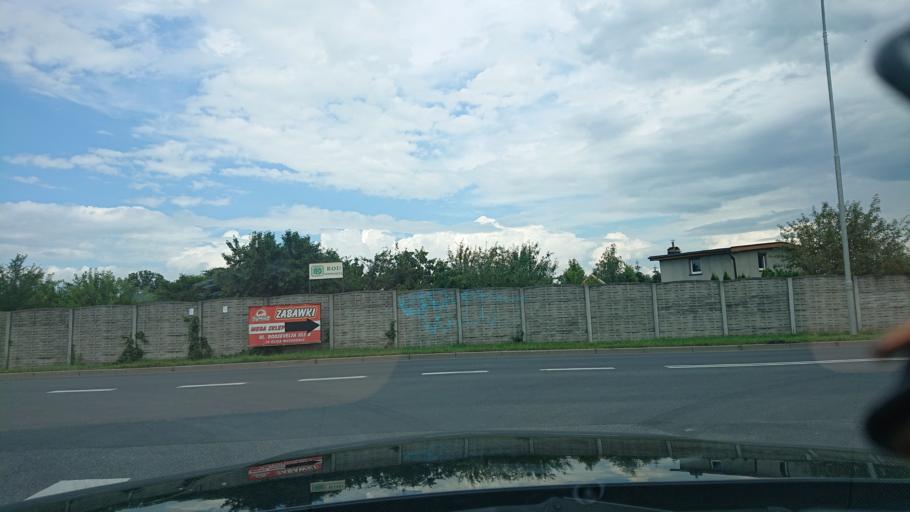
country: PL
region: Greater Poland Voivodeship
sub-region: Powiat gnieznienski
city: Gniezno
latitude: 52.5414
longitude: 17.6341
